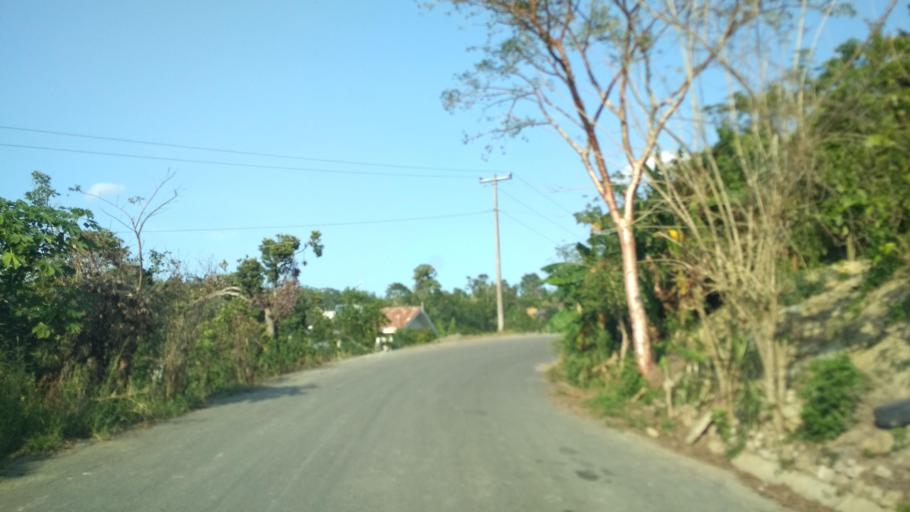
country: MX
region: Veracruz
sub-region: Poza Rica de Hidalgo
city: Arroyo del Maiz Uno
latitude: 20.4874
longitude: -97.3852
